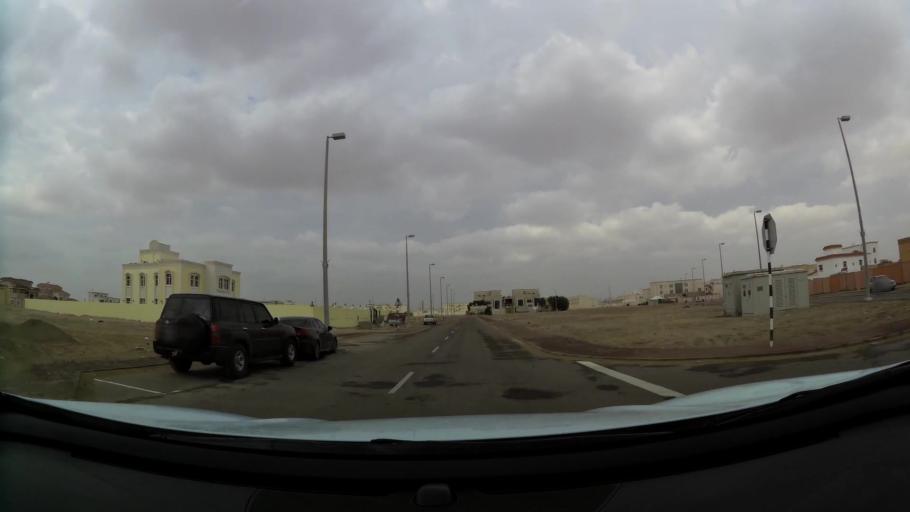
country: AE
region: Abu Dhabi
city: Abu Dhabi
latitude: 24.3450
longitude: 54.6202
